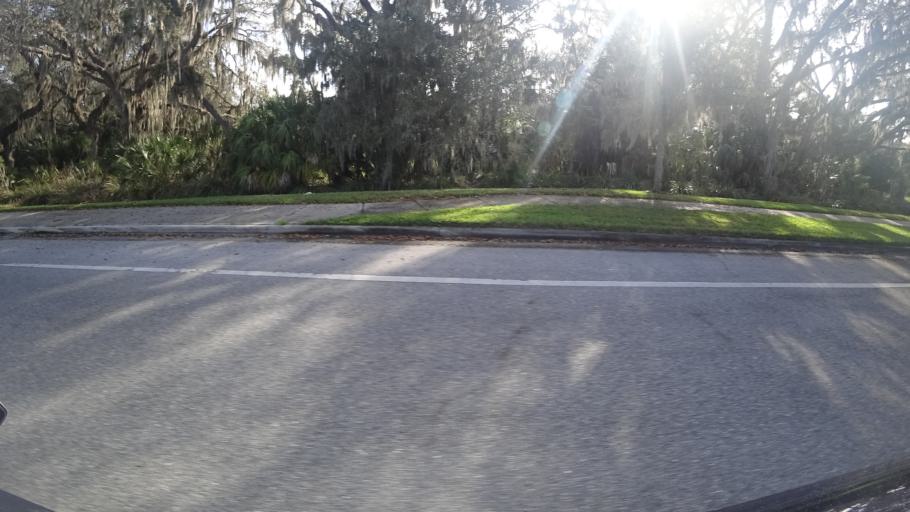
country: US
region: Florida
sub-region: Manatee County
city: Ellenton
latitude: 27.5746
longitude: -82.4686
